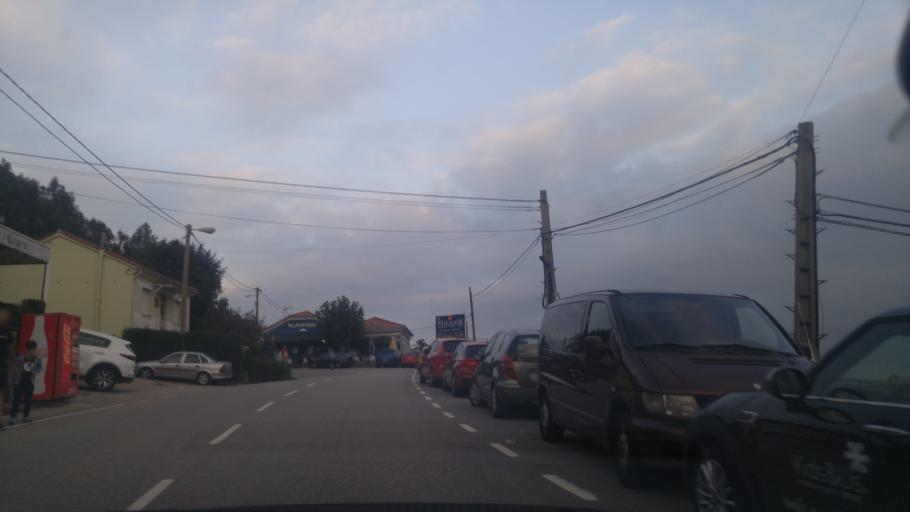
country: ES
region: Asturias
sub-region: Province of Asturias
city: Oviedo
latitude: 43.3784
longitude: -5.8639
